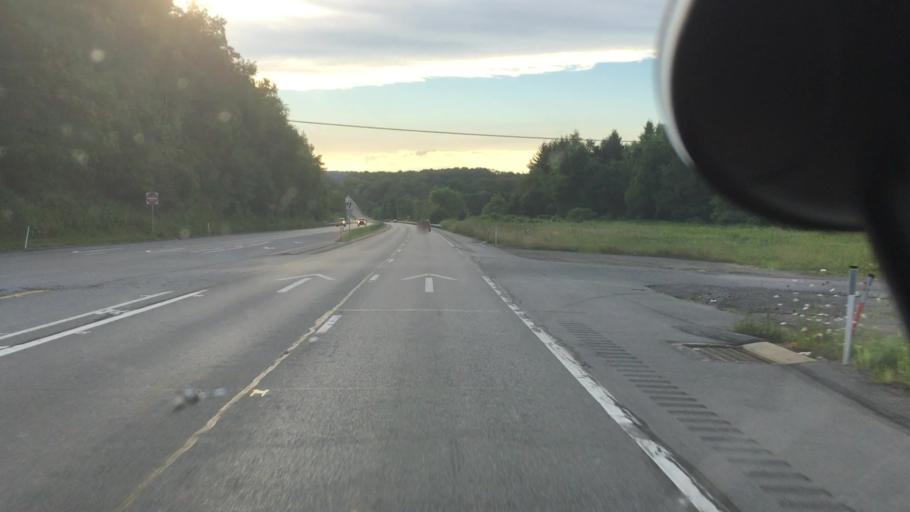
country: US
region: Pennsylvania
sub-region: Beaver County
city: Big Beaver
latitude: 40.7909
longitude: -80.4104
